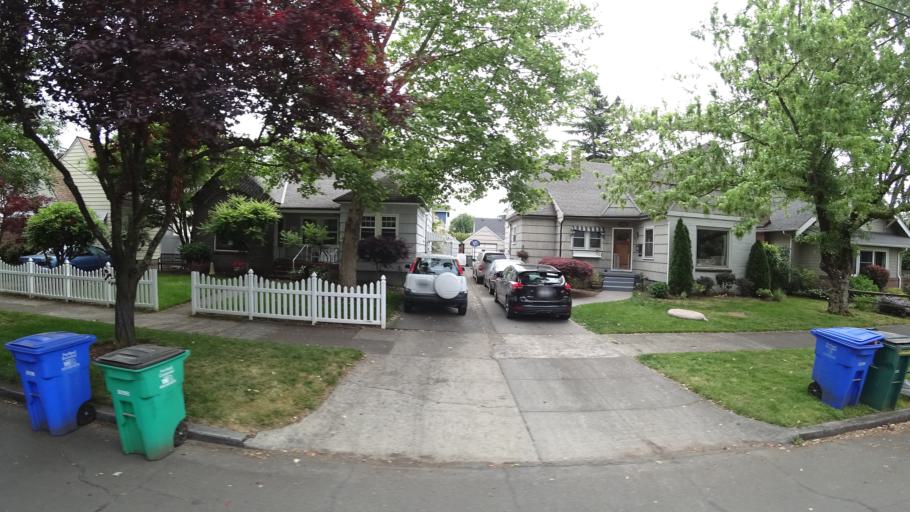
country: US
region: Oregon
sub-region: Multnomah County
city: Lents
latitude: 45.5356
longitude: -122.6079
